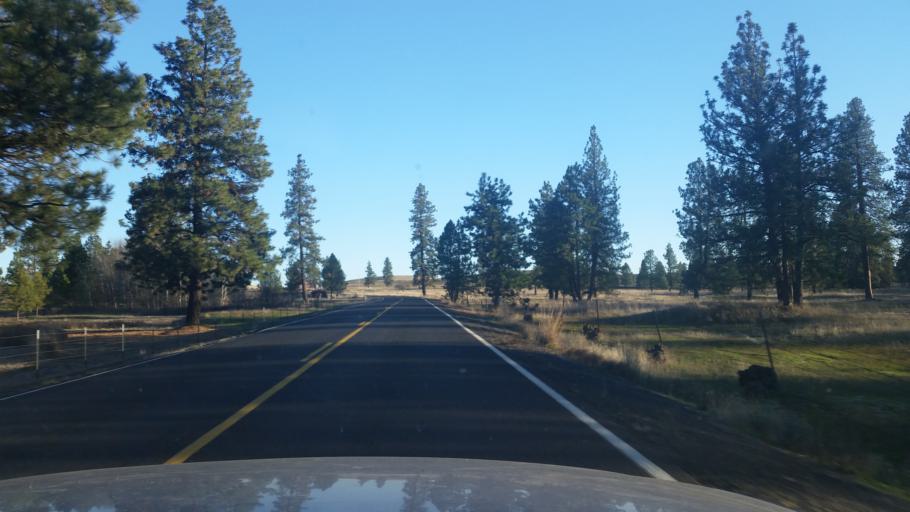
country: US
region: Washington
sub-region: Spokane County
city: Opportunity
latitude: 47.3799
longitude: -117.3119
